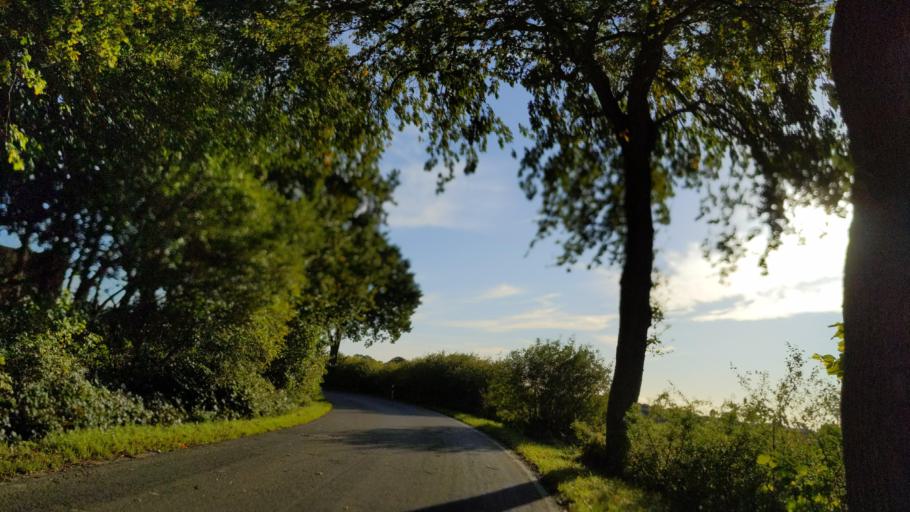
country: DE
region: Schleswig-Holstein
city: Ahrensbok
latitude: 54.0317
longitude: 10.5992
